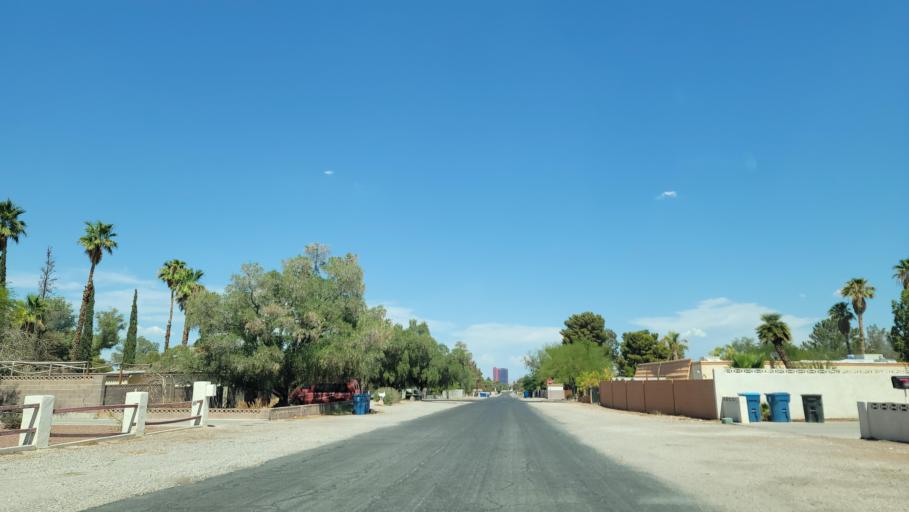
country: US
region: Nevada
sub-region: Clark County
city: Spring Valley
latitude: 36.1349
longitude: -115.2351
